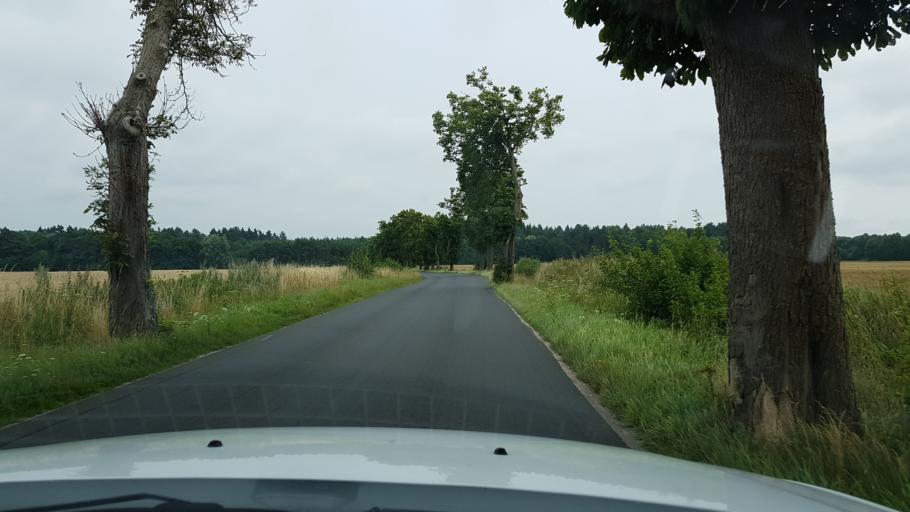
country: PL
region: West Pomeranian Voivodeship
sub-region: Powiat slawienski
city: Slawno
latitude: 54.5001
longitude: 16.5749
